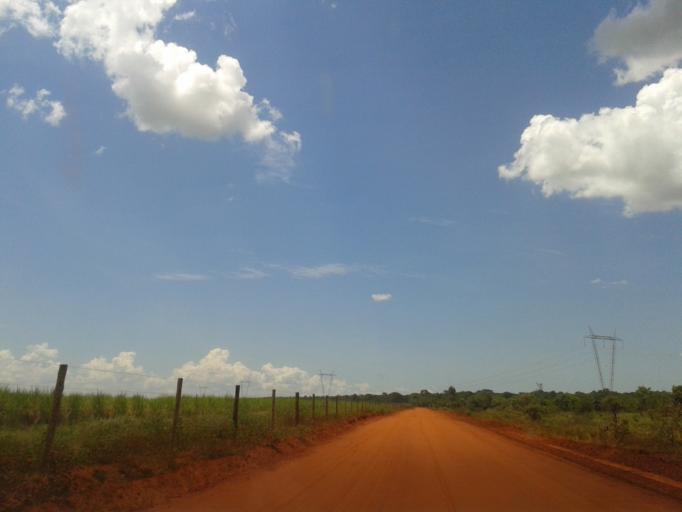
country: BR
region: Minas Gerais
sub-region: Santa Vitoria
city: Santa Vitoria
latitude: -19.1668
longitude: -50.4074
